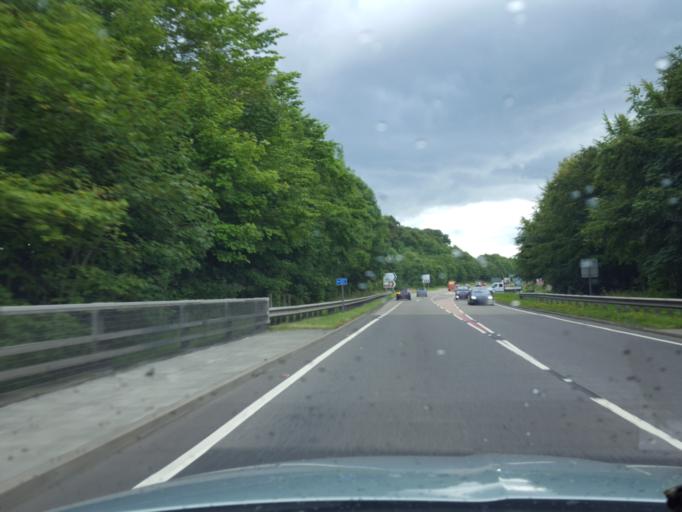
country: GB
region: Scotland
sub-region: Perth and Kinross
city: Bankfoot
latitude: 56.5614
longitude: -3.5913
